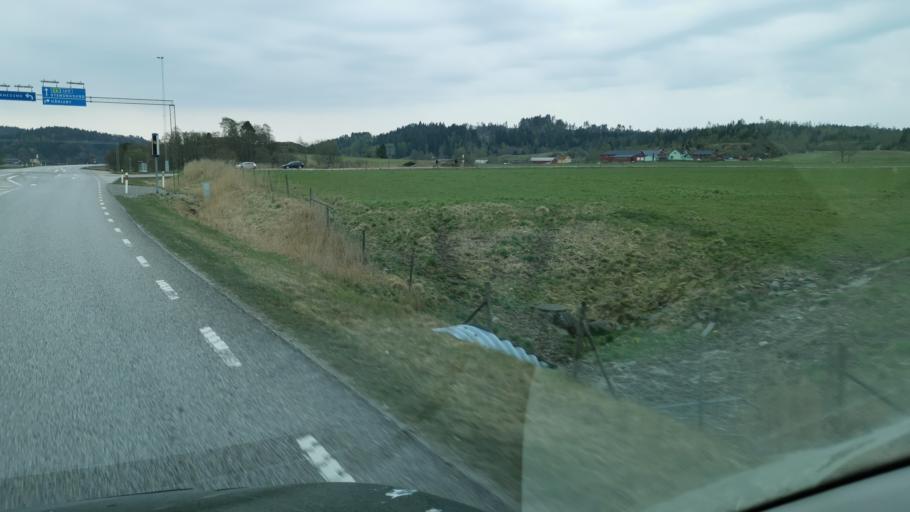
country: SE
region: Vaestra Goetaland
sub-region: Orust
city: Henan
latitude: 58.1652
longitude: 11.7045
